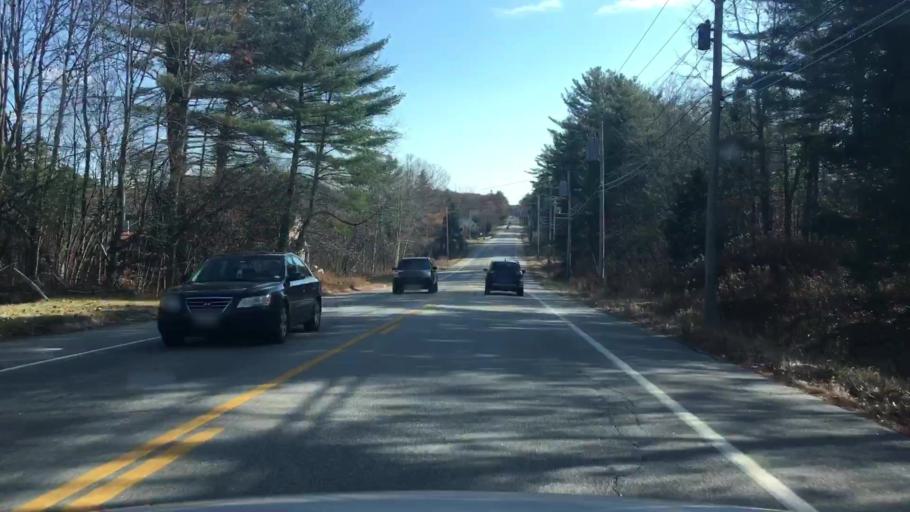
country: US
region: Maine
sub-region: Kennebec County
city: Chelsea
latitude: 44.2905
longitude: -69.7055
